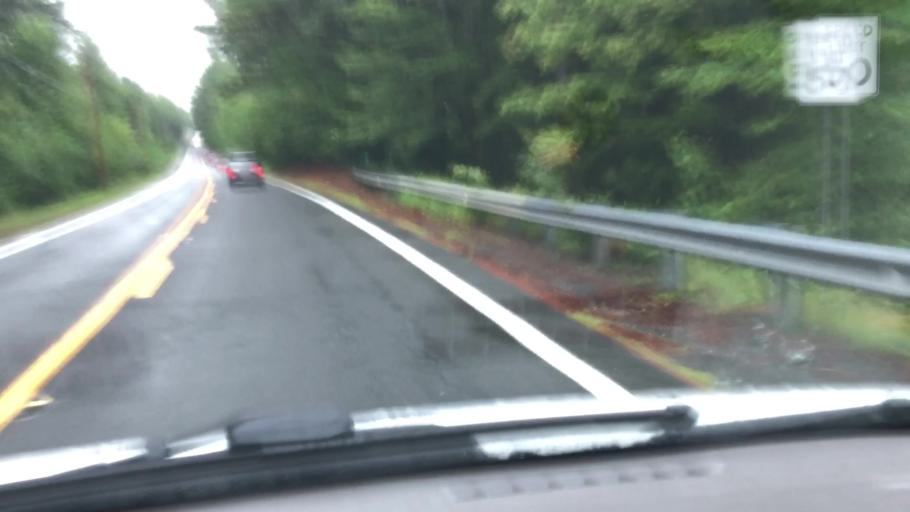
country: US
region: Massachusetts
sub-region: Hampshire County
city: Chesterfield
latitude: 42.3720
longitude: -72.9127
